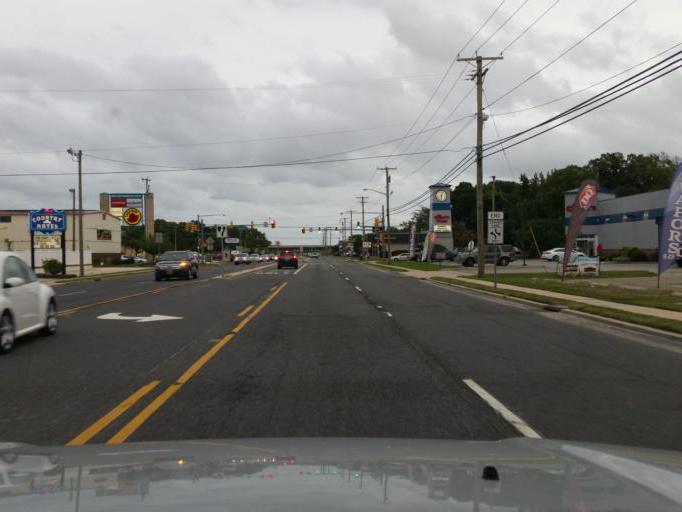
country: US
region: New Jersey
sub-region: Cape May County
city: Rio Grande
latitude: 39.0118
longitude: -74.8715
